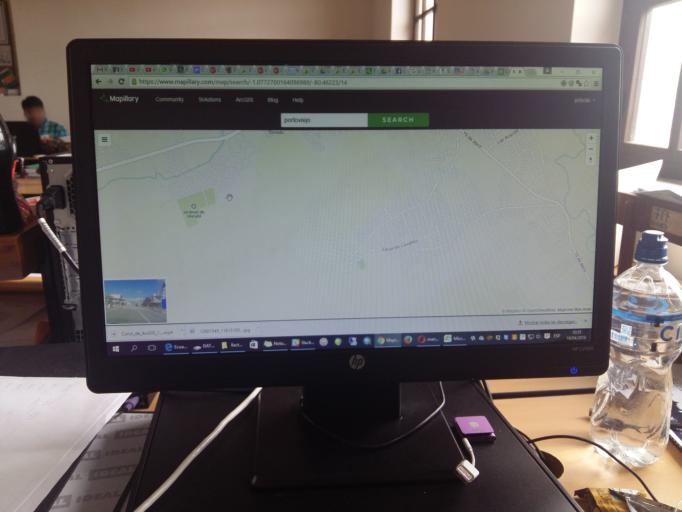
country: EC
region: Azuay
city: Cuenca
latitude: -2.9001
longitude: -79.0112
